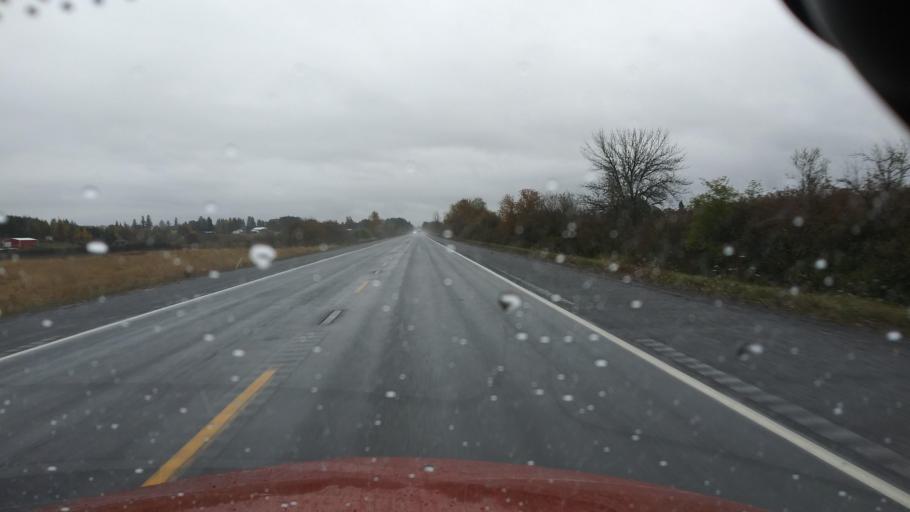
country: US
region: Oregon
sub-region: Washington County
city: Forest Grove
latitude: 45.4704
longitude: -123.1351
